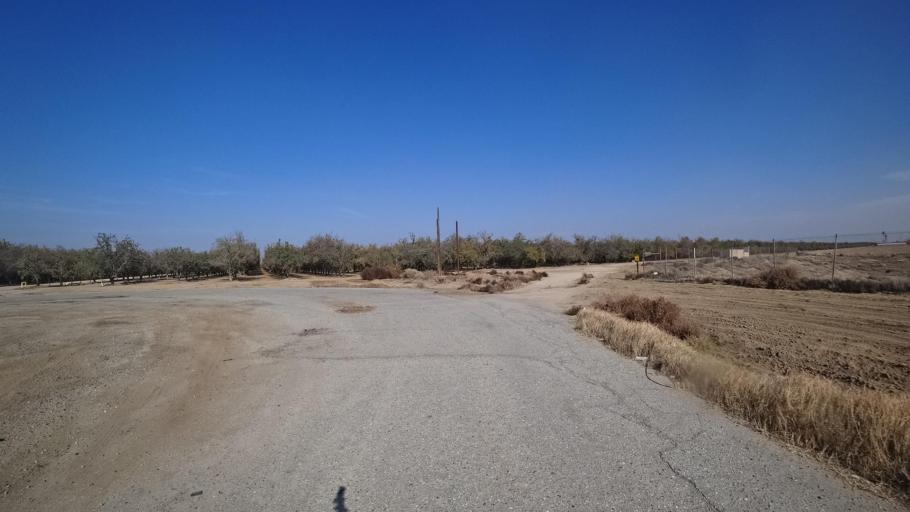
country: US
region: California
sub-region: Kern County
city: Shafter
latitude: 35.5365
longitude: -119.1867
